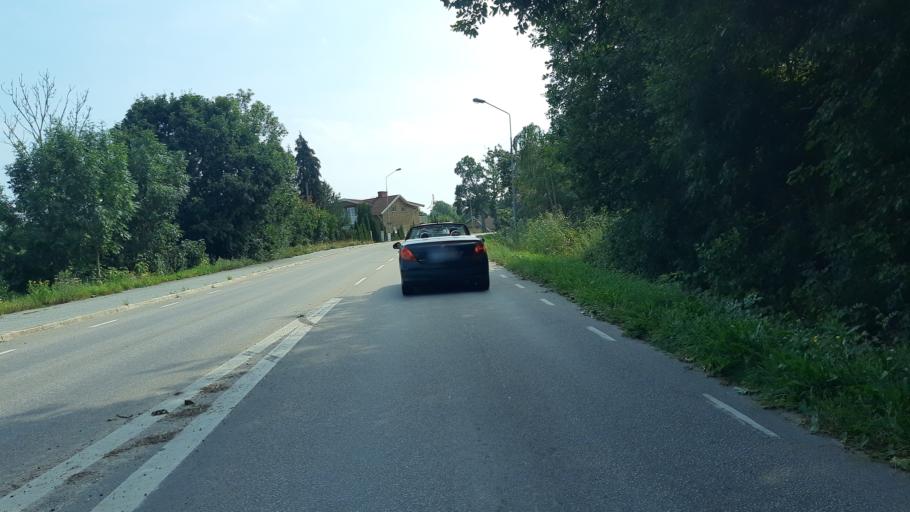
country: SE
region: Blekinge
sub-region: Karlskrona Kommun
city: Nattraby
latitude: 56.1952
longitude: 15.5350
